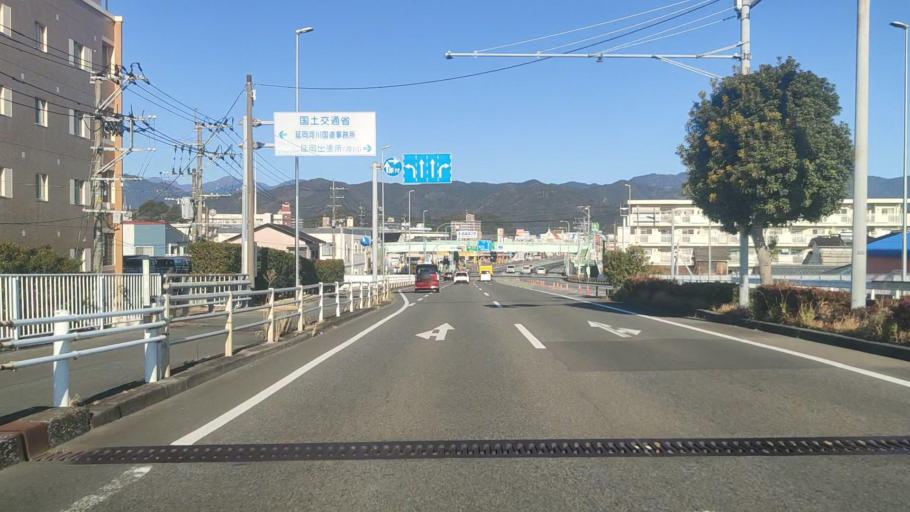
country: JP
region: Miyazaki
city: Nobeoka
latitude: 32.5853
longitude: 131.6782
